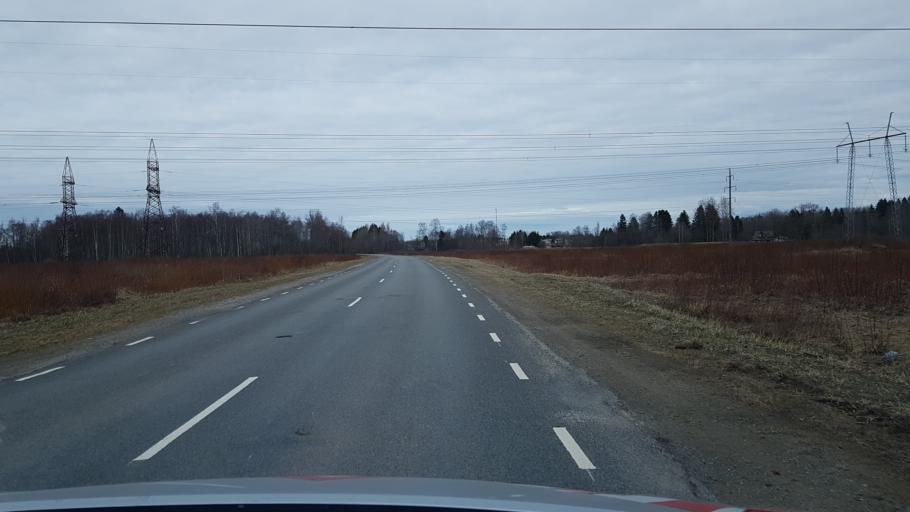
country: EE
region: Ida-Virumaa
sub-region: Sillamaee linn
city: Sillamae
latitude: 59.3633
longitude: 27.7575
